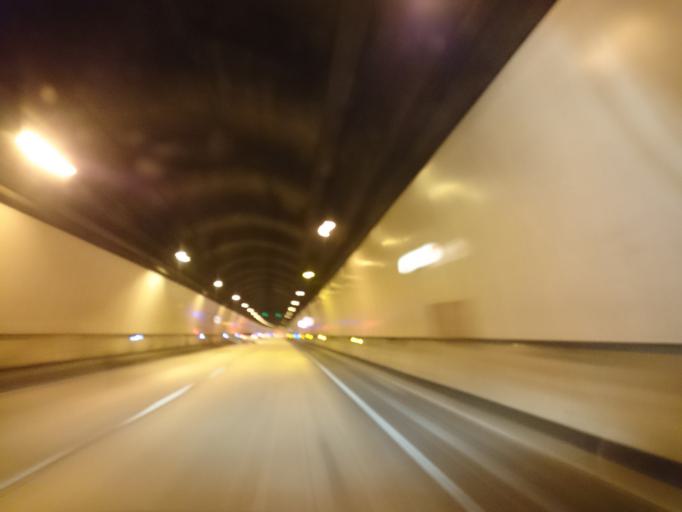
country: ES
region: Catalonia
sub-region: Provincia de Barcelona
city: Horta-Guinardo
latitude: 41.4234
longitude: 2.1582
